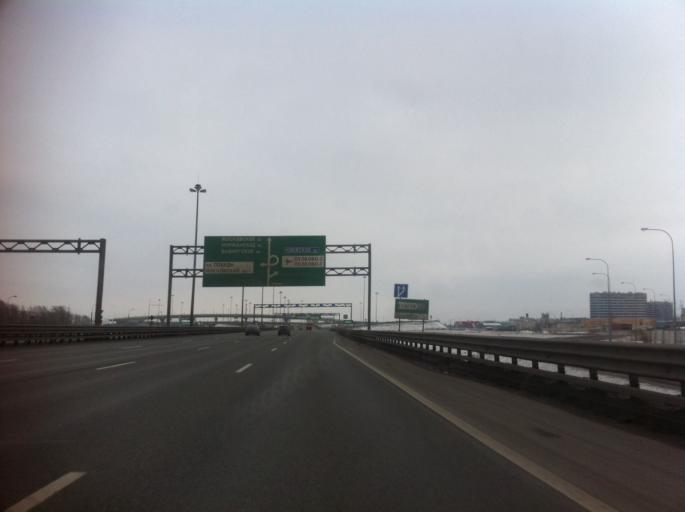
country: RU
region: St.-Petersburg
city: Kupchino
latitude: 59.8162
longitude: 30.3116
